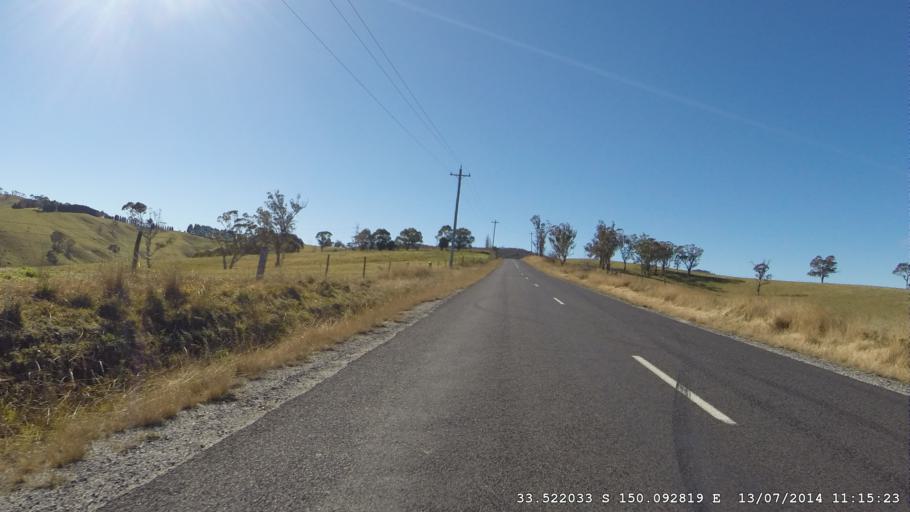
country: AU
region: New South Wales
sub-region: Lithgow
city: Bowenfels
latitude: -33.5220
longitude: 150.0928
